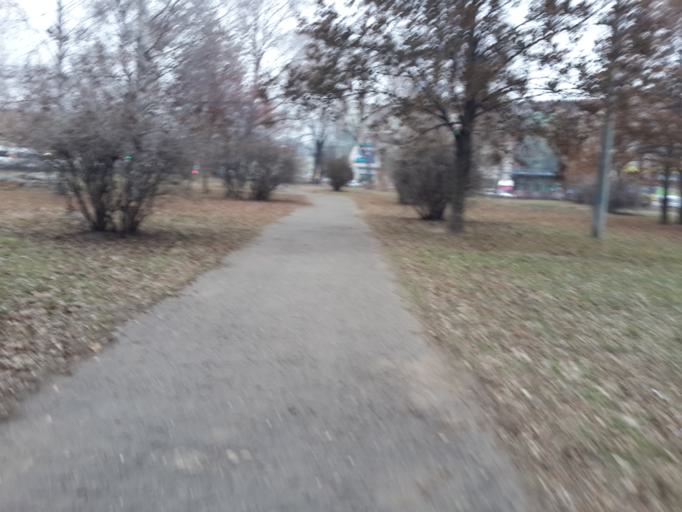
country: RU
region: Jaroslavl
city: Yaroslavl
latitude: 57.6369
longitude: 39.8806
